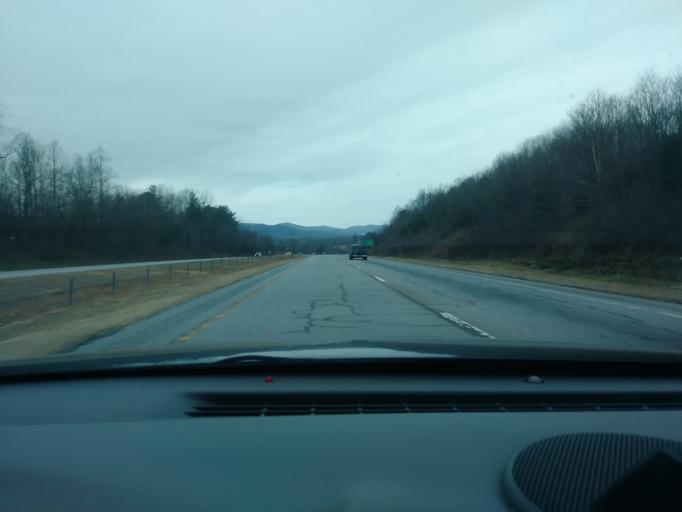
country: US
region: North Carolina
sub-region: Yadkin County
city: Jonesville
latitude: 36.1413
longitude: -80.8831
